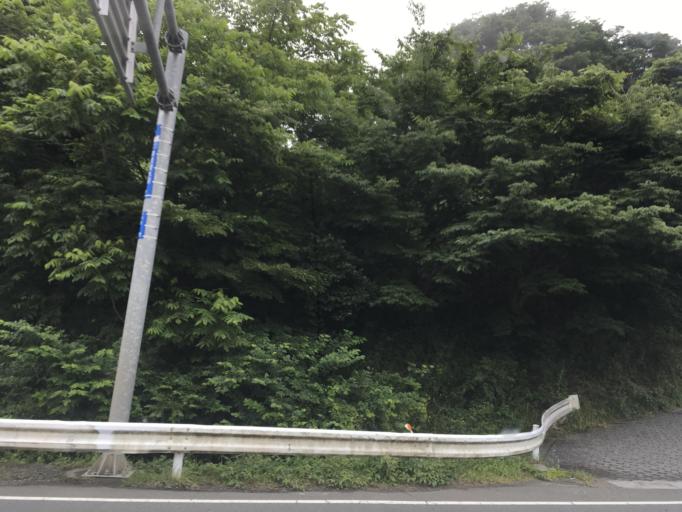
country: JP
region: Iwate
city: Ofunato
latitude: 38.9069
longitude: 141.6486
